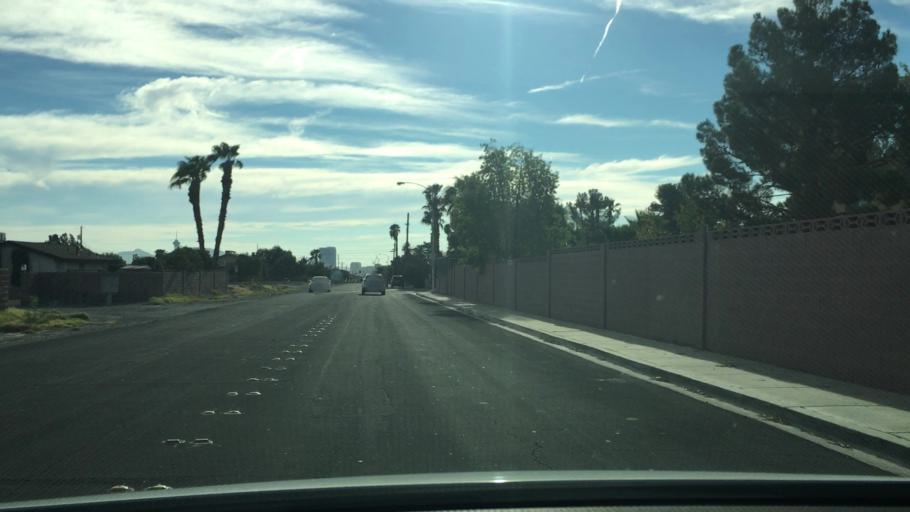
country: US
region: Nevada
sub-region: Clark County
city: Spring Valley
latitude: 36.1329
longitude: -115.2240
